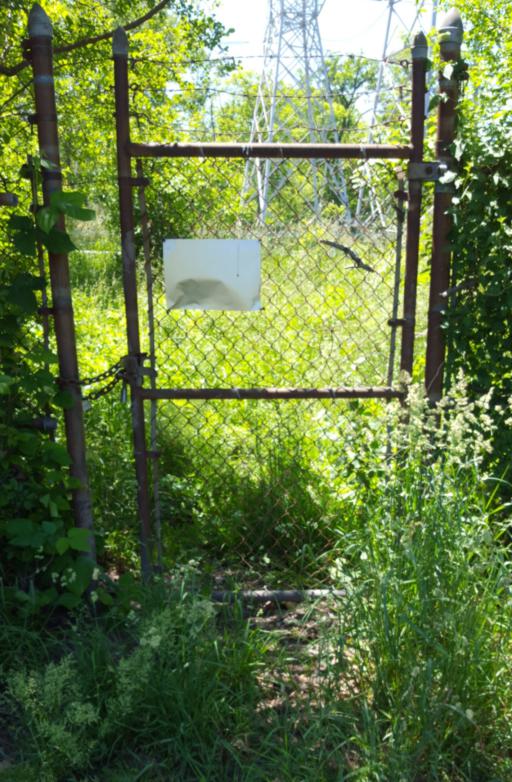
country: US
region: Illinois
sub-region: Cook County
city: Morton Grove
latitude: 42.0508
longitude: -87.7811
